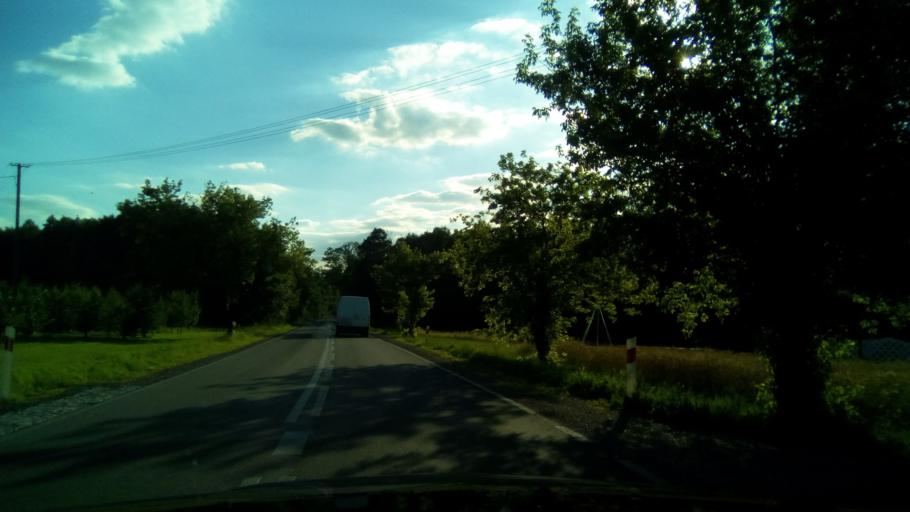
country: PL
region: Masovian Voivodeship
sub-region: Powiat bialobrzeski
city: Stromiec
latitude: 51.6495
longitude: 21.1214
